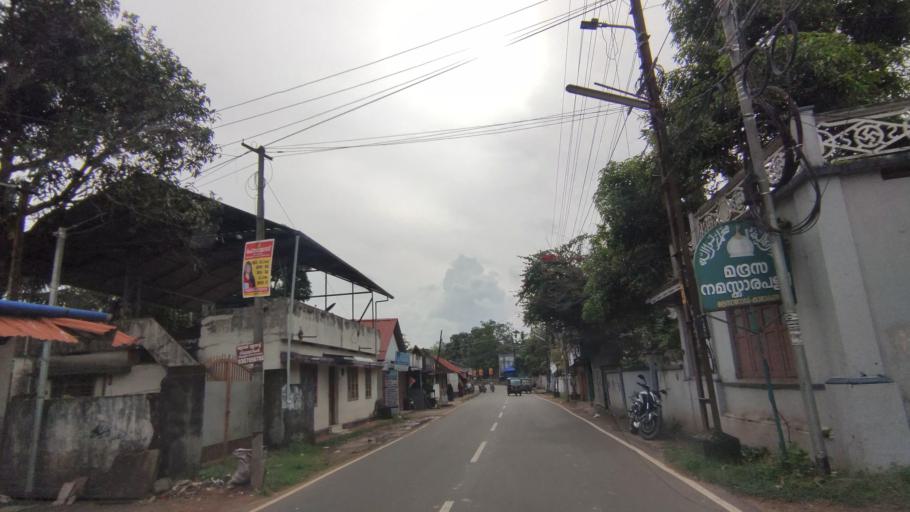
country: IN
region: Kerala
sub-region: Kottayam
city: Kottayam
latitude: 9.5845
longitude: 76.5152
